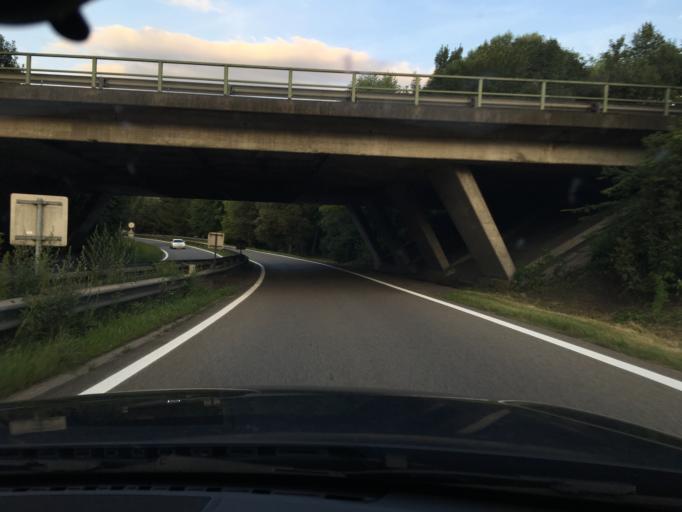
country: AT
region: Vorarlberg
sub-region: Politischer Bezirk Dornbirn
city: Hohenems
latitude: 47.3751
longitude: 9.6697
